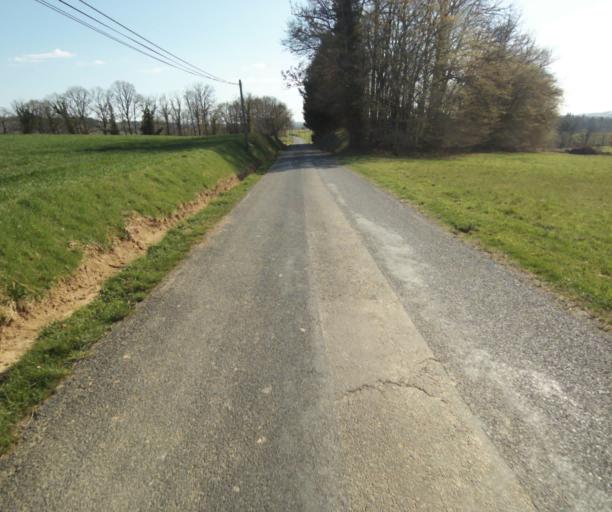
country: FR
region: Limousin
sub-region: Departement de la Correze
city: Saint-Mexant
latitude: 45.3033
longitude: 1.6170
